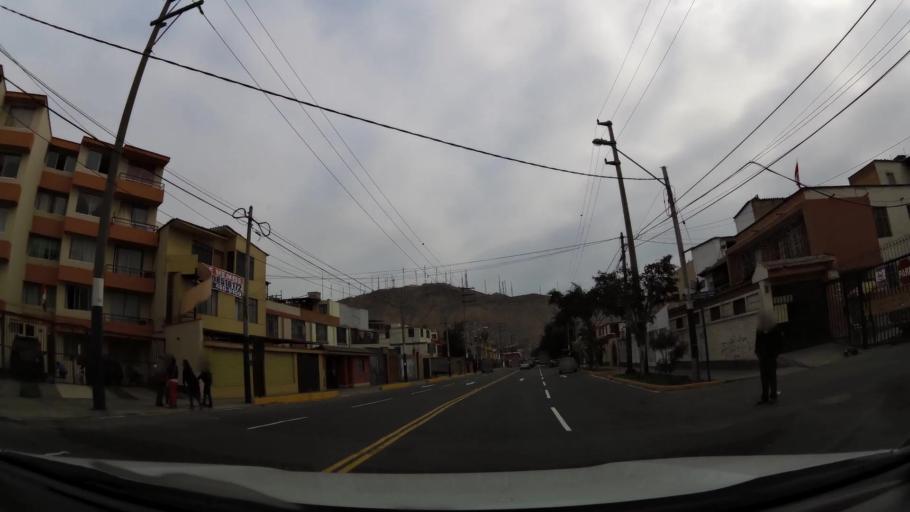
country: PE
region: Lima
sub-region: Lima
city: Surco
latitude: -12.1717
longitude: -77.0188
